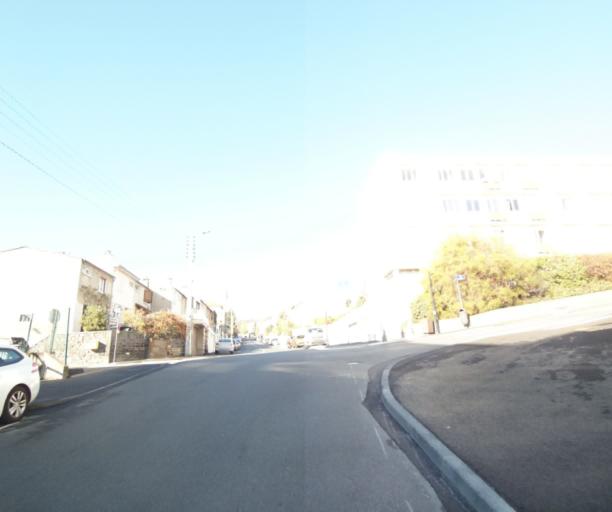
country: FR
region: Auvergne
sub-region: Departement du Puy-de-Dome
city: Chamalieres
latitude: 45.7873
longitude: 3.0685
